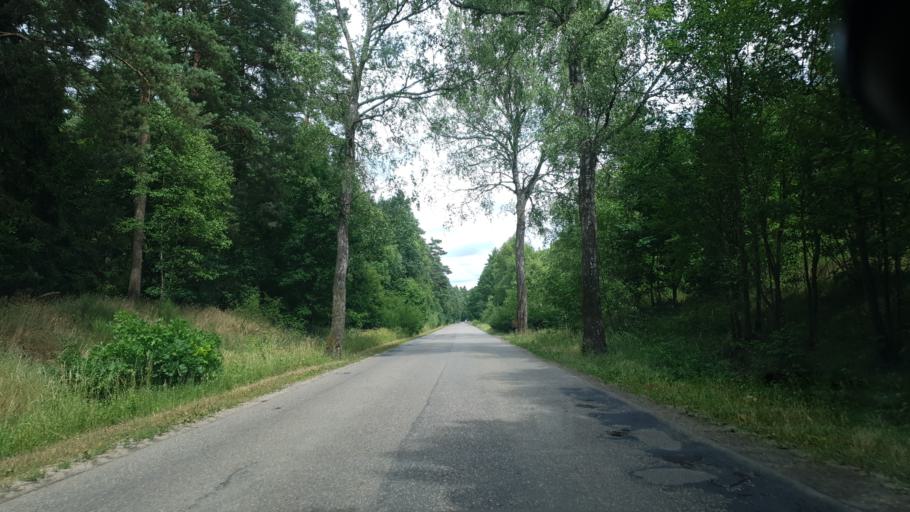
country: PL
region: Pomeranian Voivodeship
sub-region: Powiat kartuski
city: Stezyca
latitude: 54.2589
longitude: 18.0327
